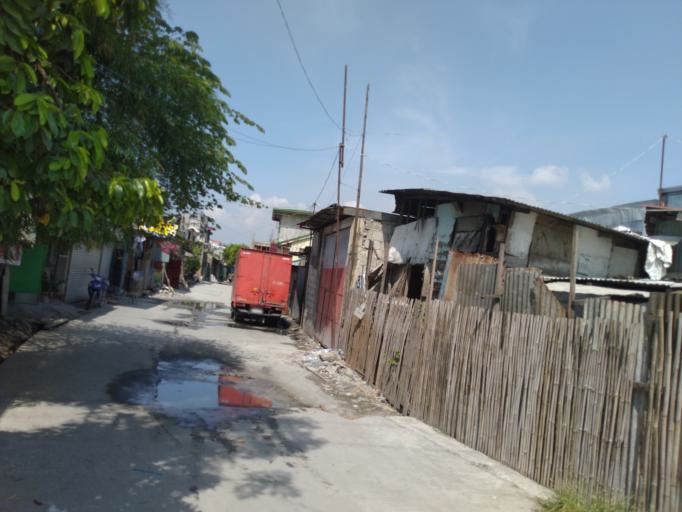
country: PH
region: Calabarzon
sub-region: Province of Rizal
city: Taytay
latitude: 14.5369
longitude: 121.1119
